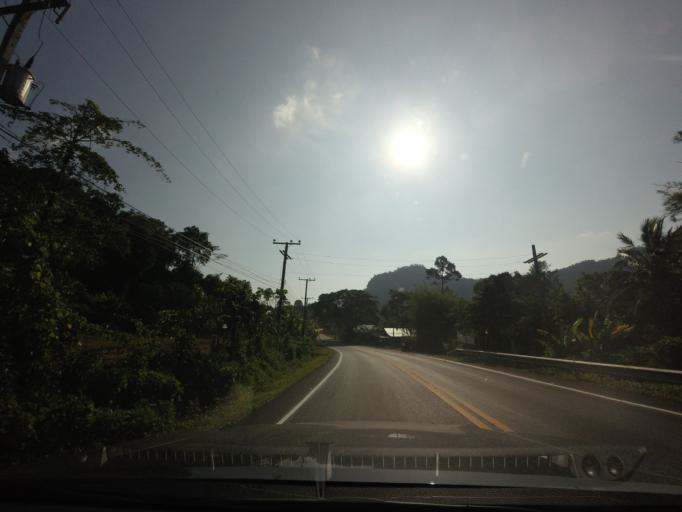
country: TH
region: Phetchabun
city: Lom Kao
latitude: 16.8687
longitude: 101.1367
